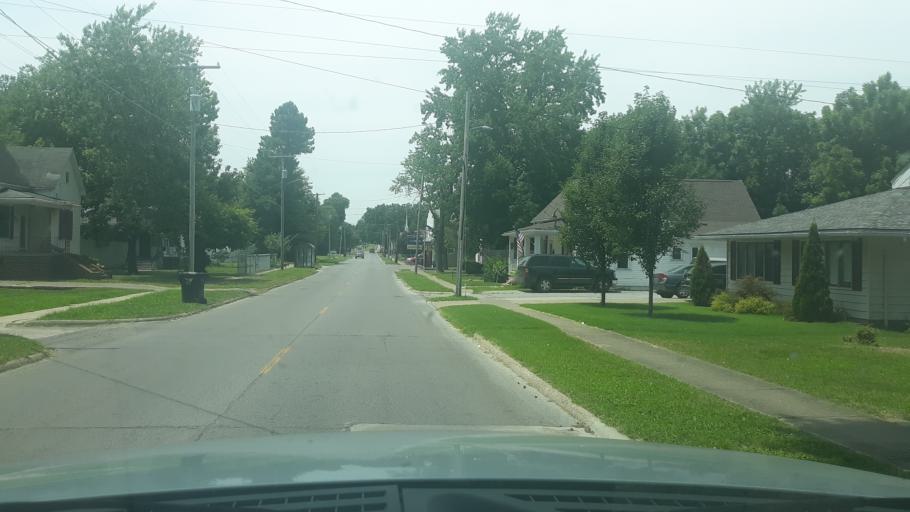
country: US
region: Illinois
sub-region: Saline County
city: Harrisburg
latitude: 37.7313
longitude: -88.5499
